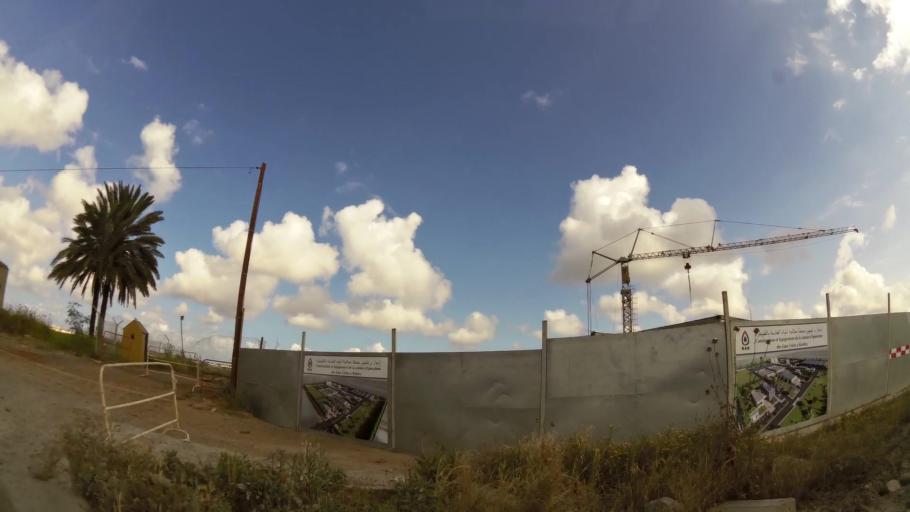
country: MA
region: Gharb-Chrarda-Beni Hssen
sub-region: Kenitra Province
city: Kenitra
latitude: 34.2718
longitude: -6.5653
